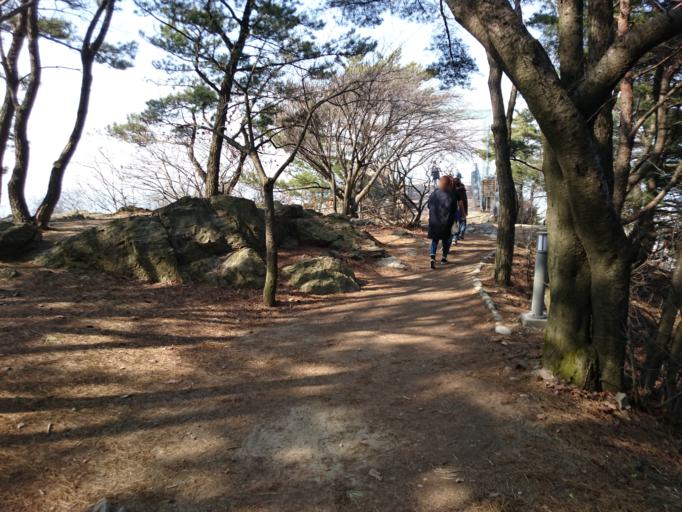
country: KR
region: Daegu
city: Daegu
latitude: 35.8244
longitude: 128.5795
